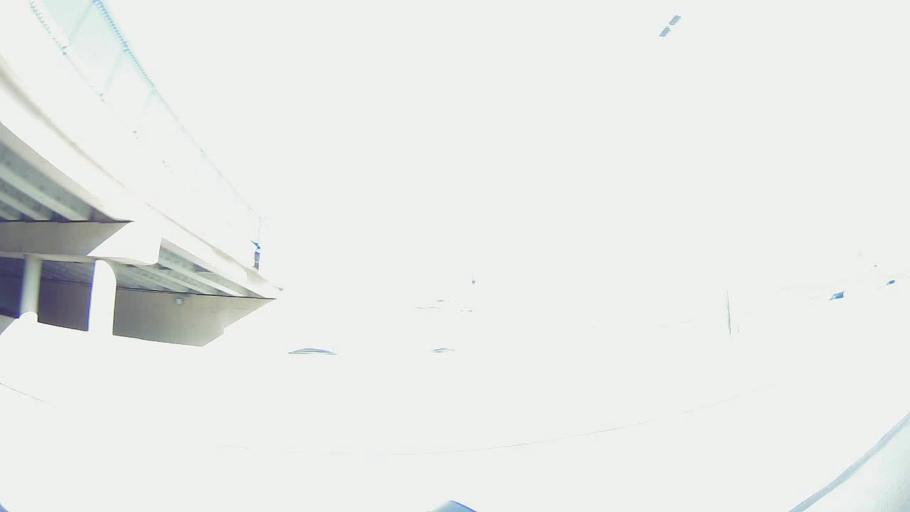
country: US
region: Michigan
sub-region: Wayne County
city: Dearborn
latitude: 42.3576
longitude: -83.2166
